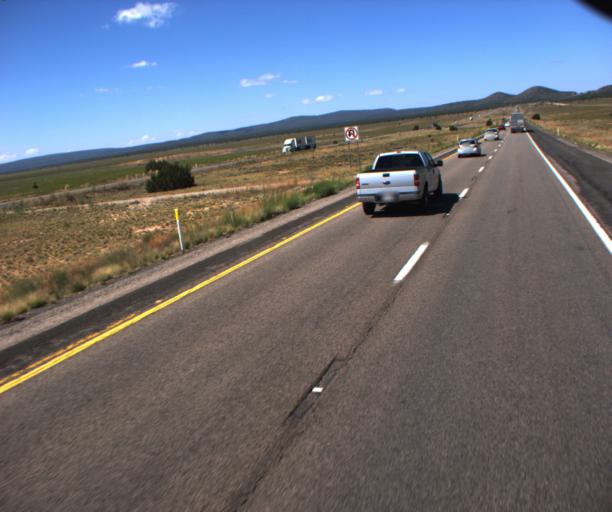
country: US
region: Arizona
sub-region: Mohave County
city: Peach Springs
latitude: 35.3141
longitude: -112.9694
